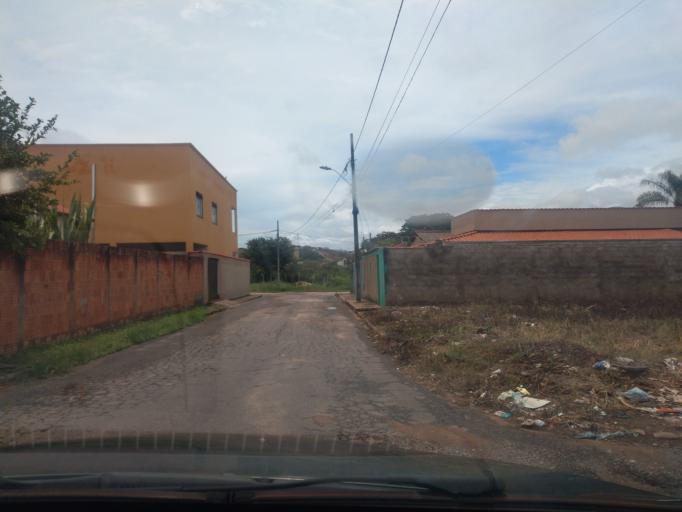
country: BR
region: Minas Gerais
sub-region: Tres Coracoes
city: Tres Coracoes
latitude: -21.6789
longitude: -45.2591
